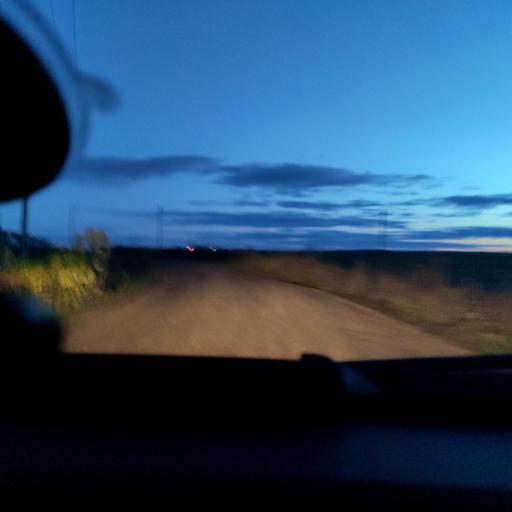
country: RU
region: Bashkortostan
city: Avdon
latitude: 54.6865
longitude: 55.7799
